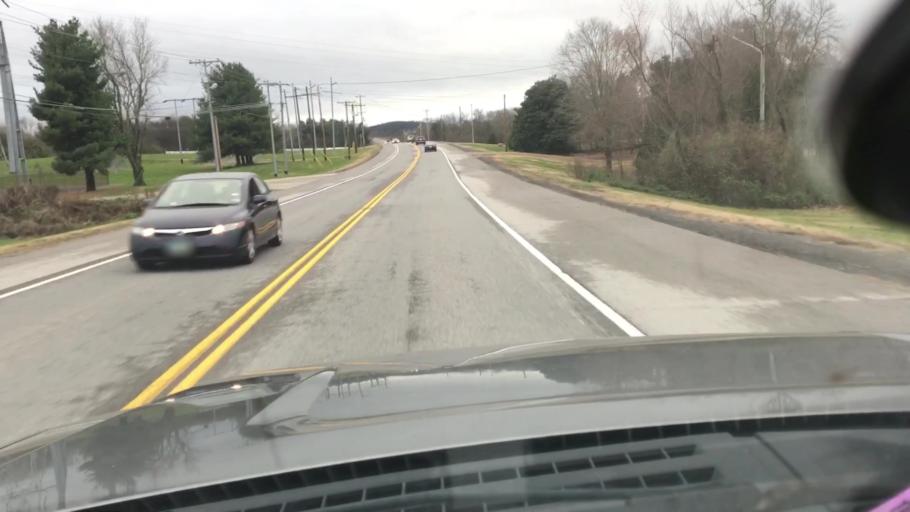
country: US
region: Tennessee
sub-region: Williamson County
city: Brentwood Estates
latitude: 35.9683
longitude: -86.7732
